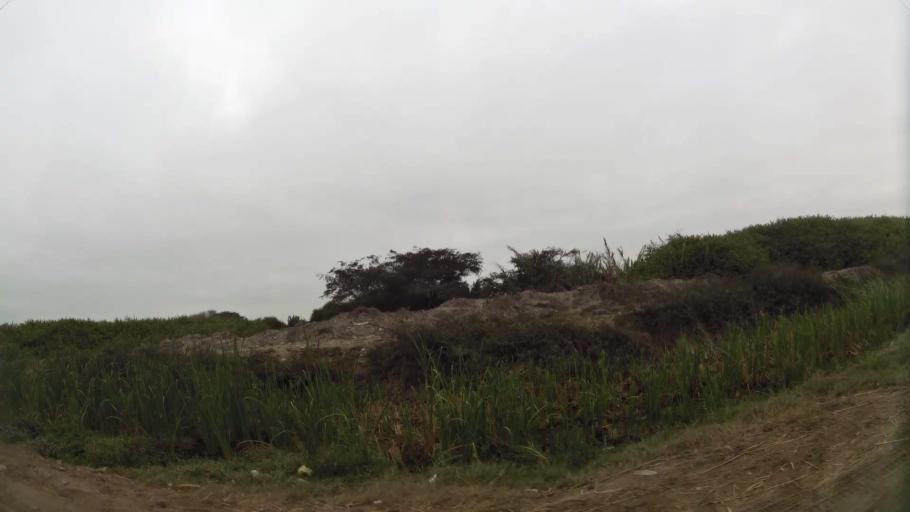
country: PE
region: Ica
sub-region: Provincia de Pisco
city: Pisco
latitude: -13.7371
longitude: -76.1974
